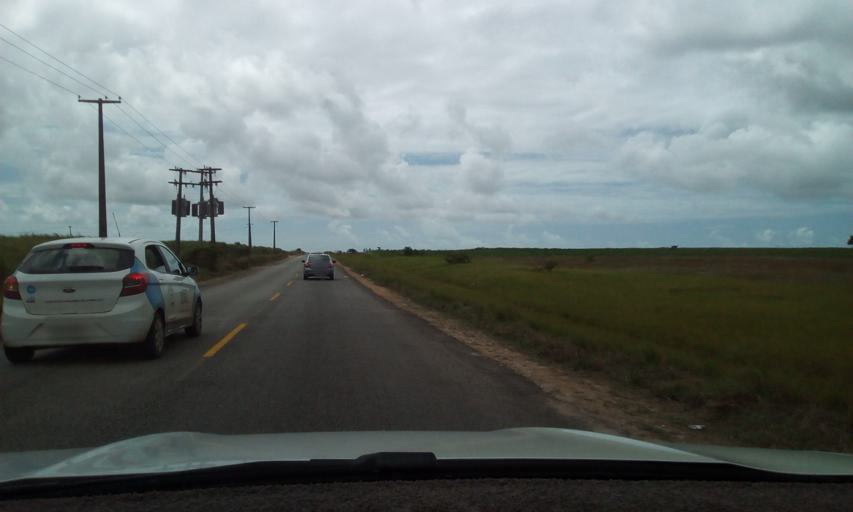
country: BR
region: Paraiba
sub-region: Rio Tinto
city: Rio Tinto
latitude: -6.7814
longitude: -35.0551
